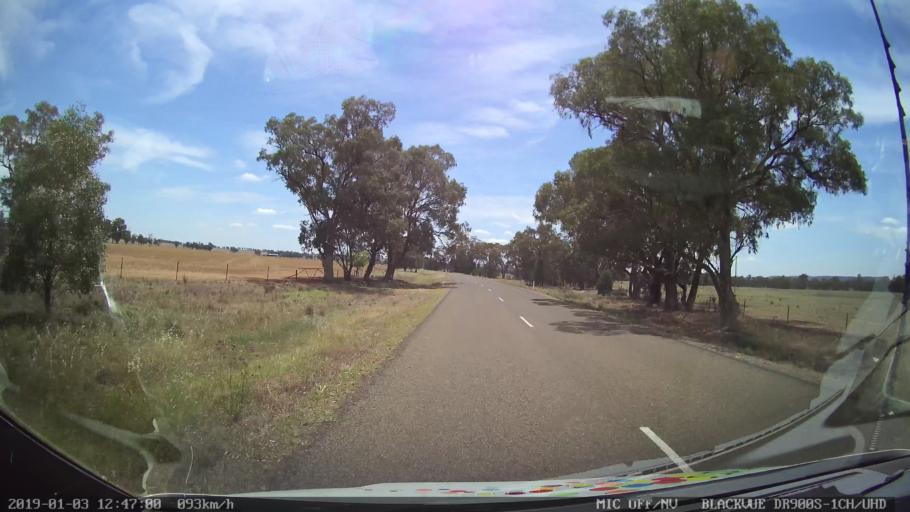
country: AU
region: New South Wales
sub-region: Weddin
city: Grenfell
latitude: -33.7329
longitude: 148.2399
